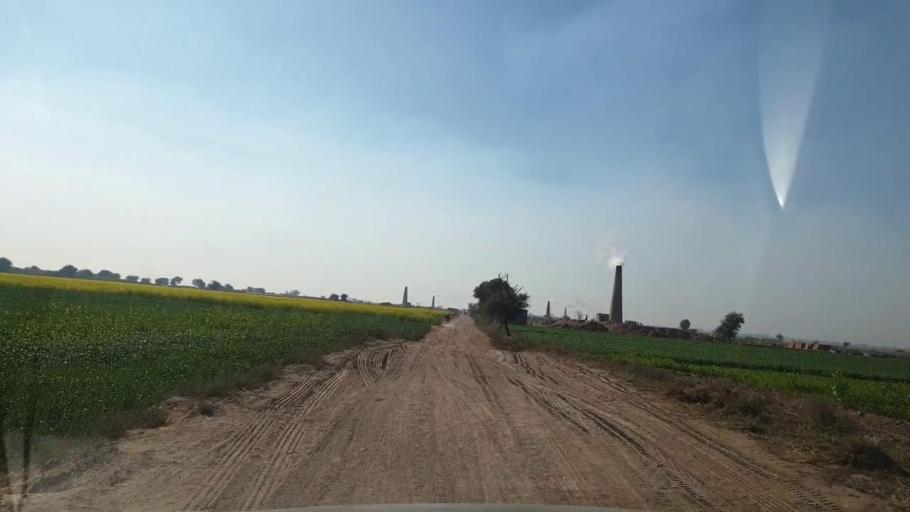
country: PK
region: Sindh
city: Jhol
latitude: 25.8049
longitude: 69.0081
